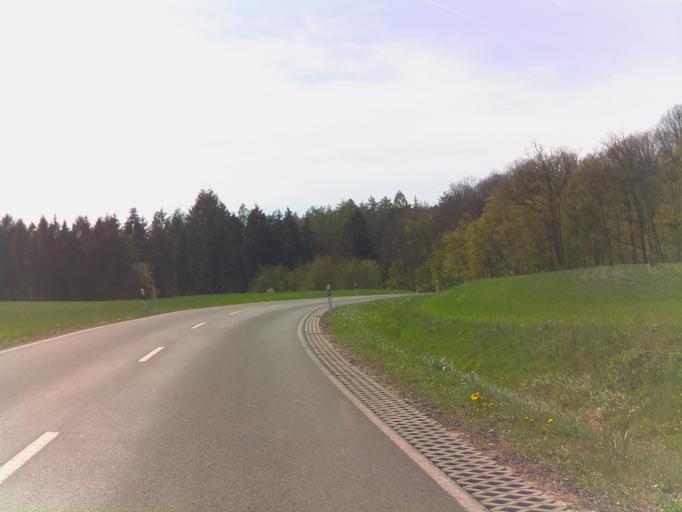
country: DE
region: Bavaria
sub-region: Regierungsbezirk Unterfranken
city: Hofheim in Unterfranken
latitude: 50.1579
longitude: 10.5634
